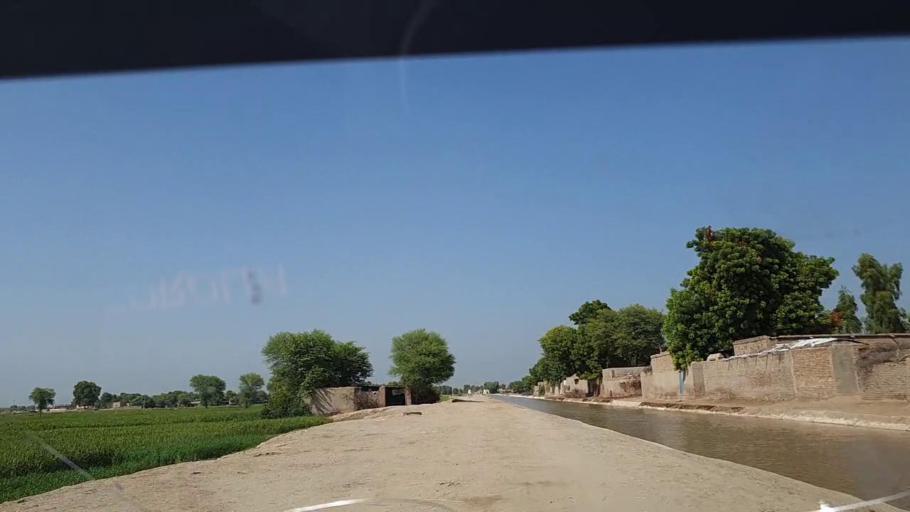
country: PK
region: Sindh
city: Ghauspur
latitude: 28.1702
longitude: 69.0978
